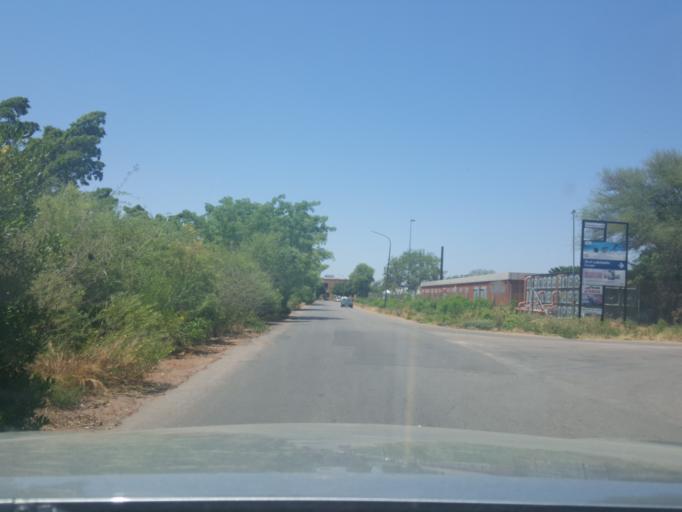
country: BW
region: South East
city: Gaborone
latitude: -24.6806
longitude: 25.8894
